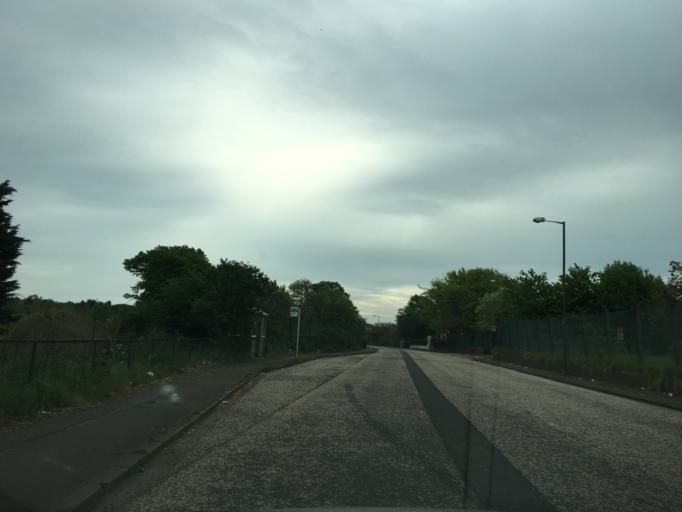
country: GB
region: Scotland
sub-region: Edinburgh
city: Ratho
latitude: 55.9519
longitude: -3.3481
